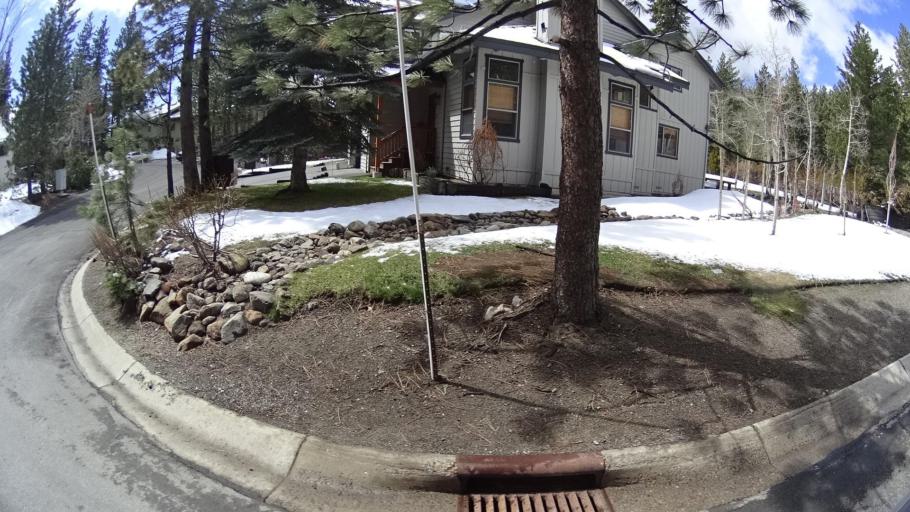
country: US
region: Nevada
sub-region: Washoe County
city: Incline Village
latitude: 39.2656
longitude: -119.9452
